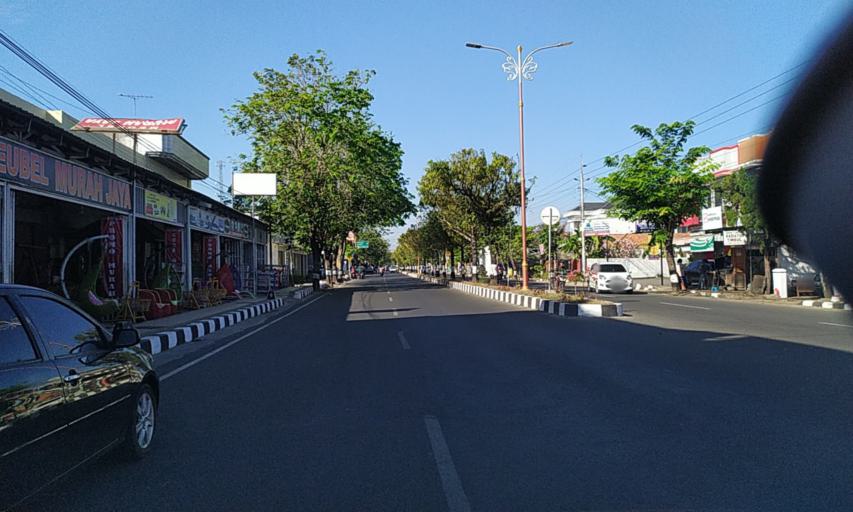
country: ID
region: Central Java
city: Rejanegara
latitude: -7.6942
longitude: 109.0320
